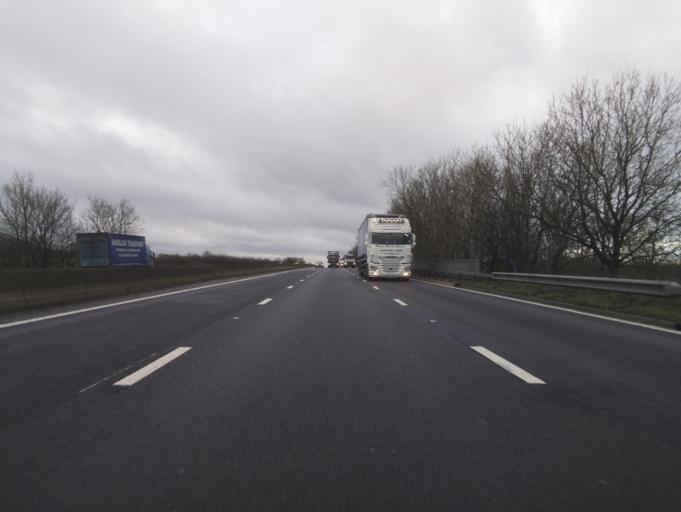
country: GB
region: England
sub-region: Lancashire
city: Lancaster
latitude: 54.0394
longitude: -2.7723
